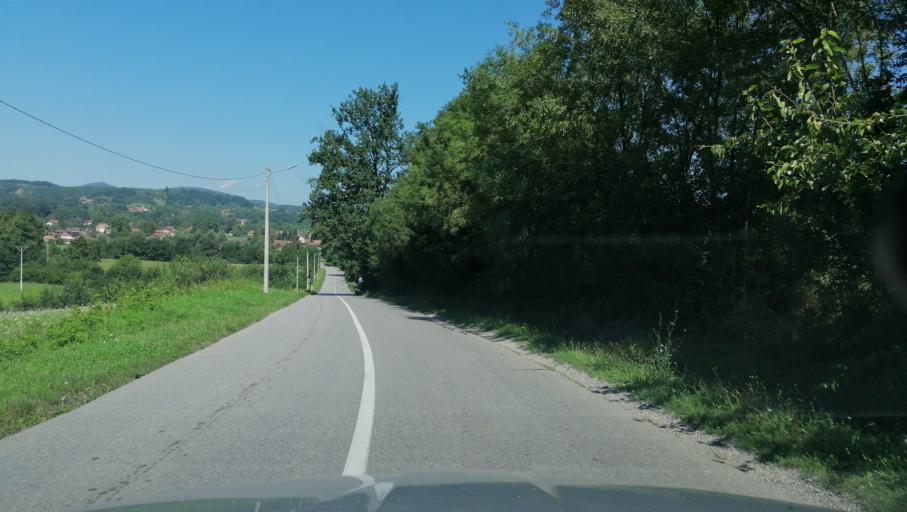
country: RS
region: Central Serbia
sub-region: Raski Okrug
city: Kraljevo
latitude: 43.7210
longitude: 20.8059
